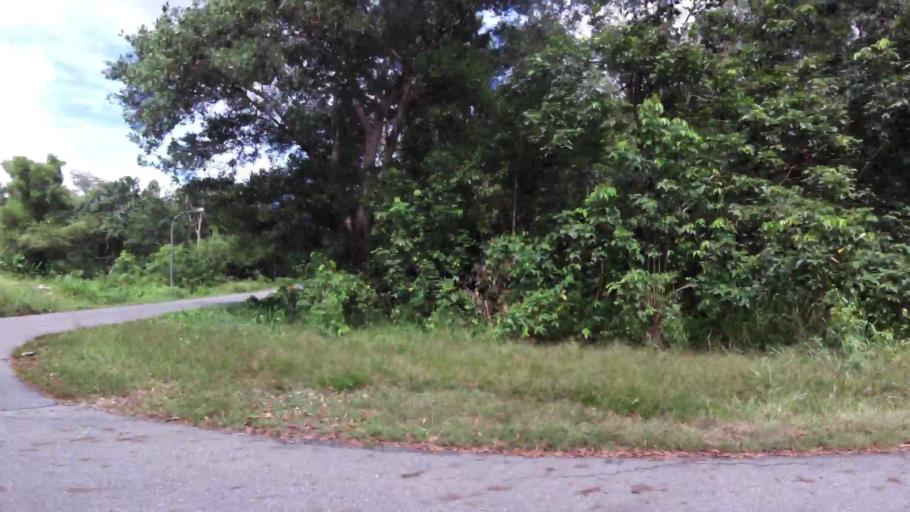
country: BN
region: Brunei and Muara
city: Bandar Seri Begawan
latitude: 4.9374
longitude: 114.9051
